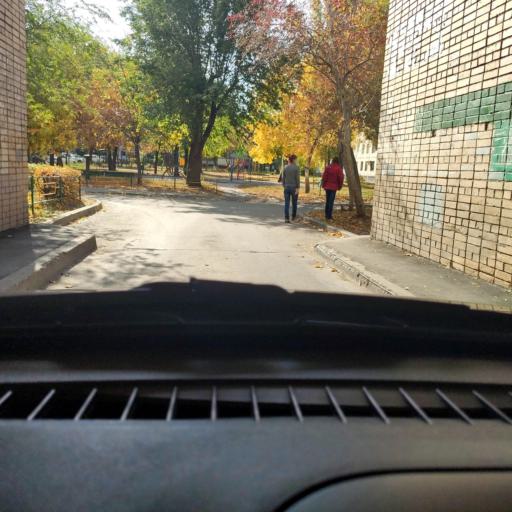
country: RU
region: Samara
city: Tol'yatti
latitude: 53.5236
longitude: 49.2943
